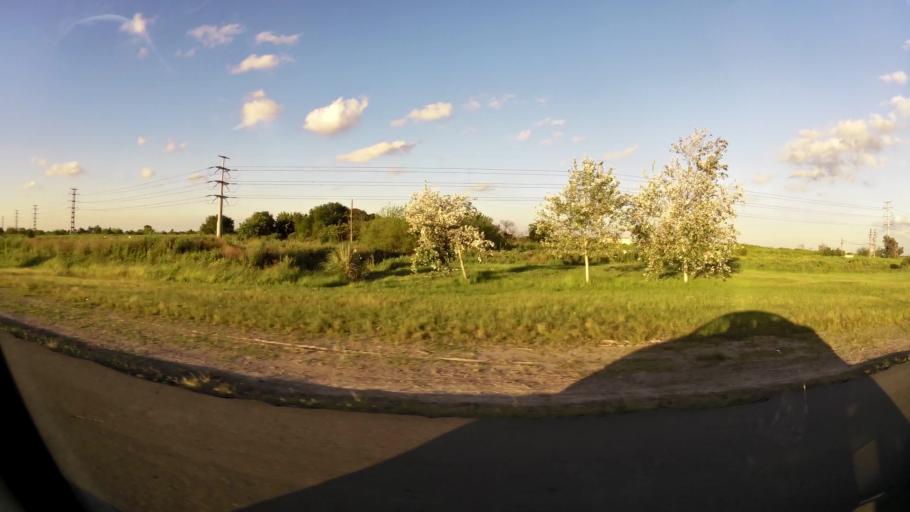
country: AR
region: Buenos Aires
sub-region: Partido de Quilmes
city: Quilmes
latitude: -34.7838
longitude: -58.1503
